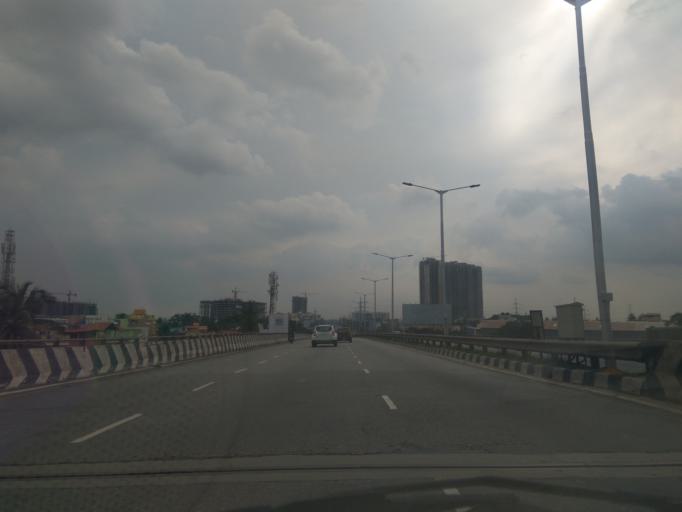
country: IN
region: Karnataka
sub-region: Bangalore Rural
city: Hoskote
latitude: 13.0261
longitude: 77.7203
